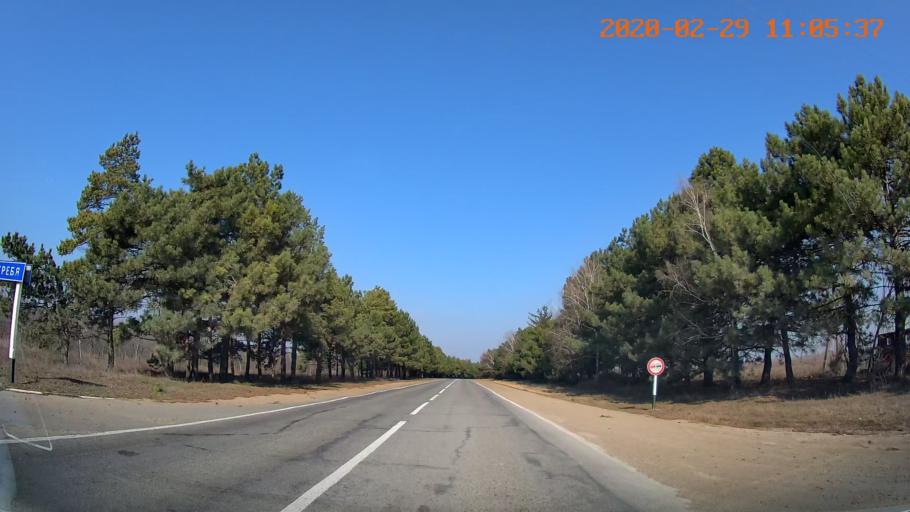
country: MD
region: Criuleni
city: Criuleni
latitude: 47.2043
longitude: 29.1911
